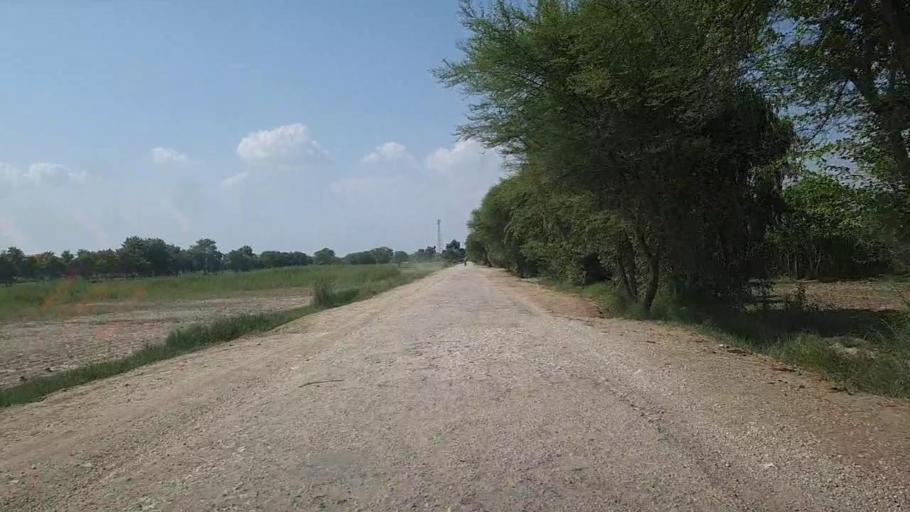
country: PK
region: Sindh
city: Khairpur
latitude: 28.1146
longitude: 69.6185
